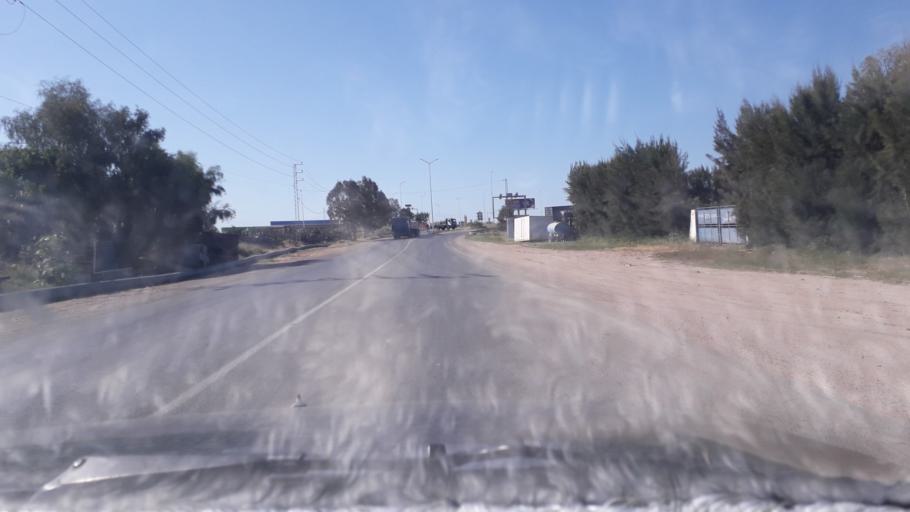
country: TN
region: Safaqis
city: Al Qarmadah
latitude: 34.8582
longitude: 10.7596
